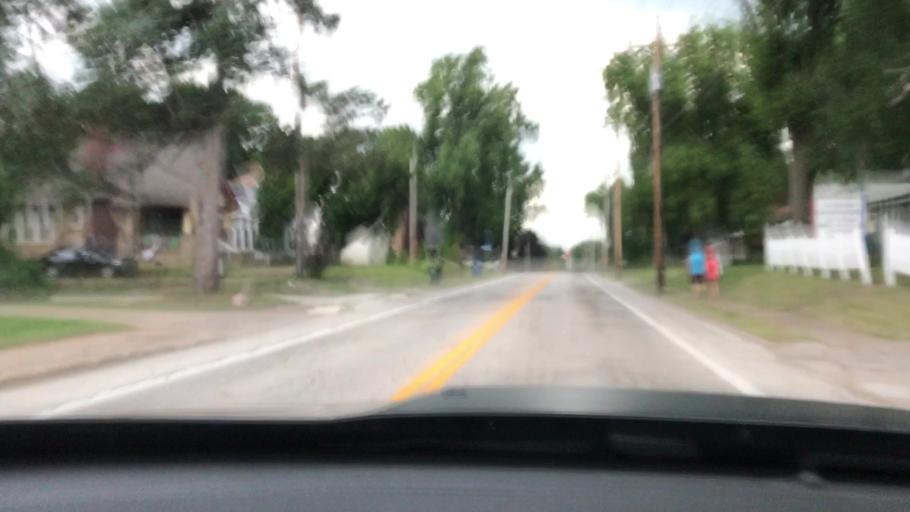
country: US
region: Iowa
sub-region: Scott County
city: Bettendorf
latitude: 41.5429
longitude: -90.5418
